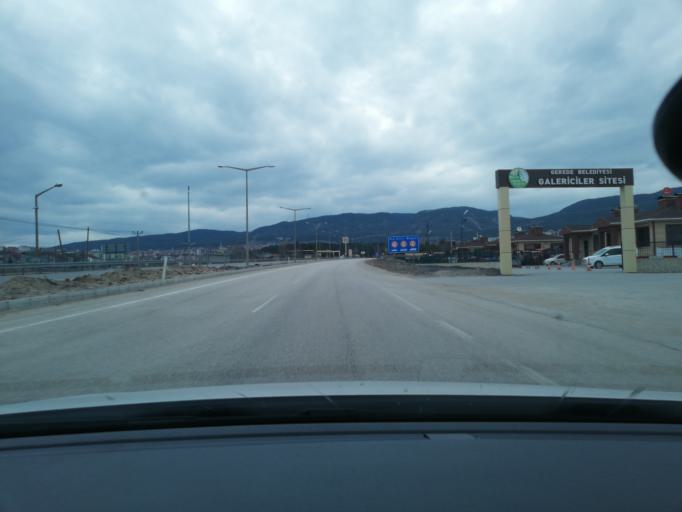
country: TR
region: Bolu
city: Gerede
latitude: 40.7841
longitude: 32.2113
